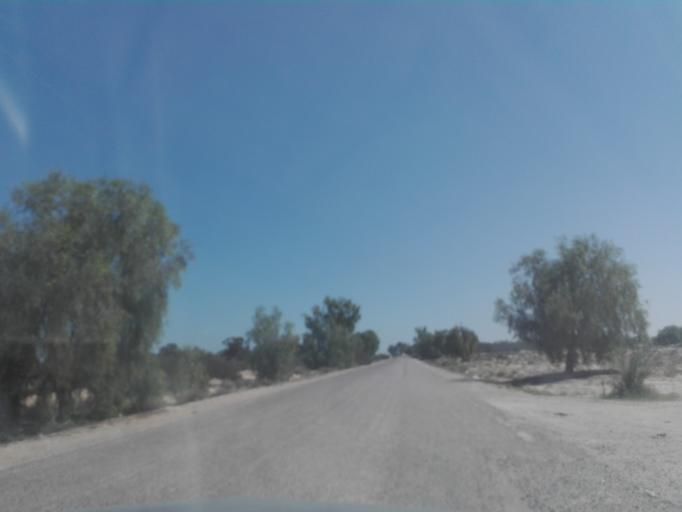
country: TN
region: Qabis
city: Gabes
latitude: 33.8724
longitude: 10.0337
